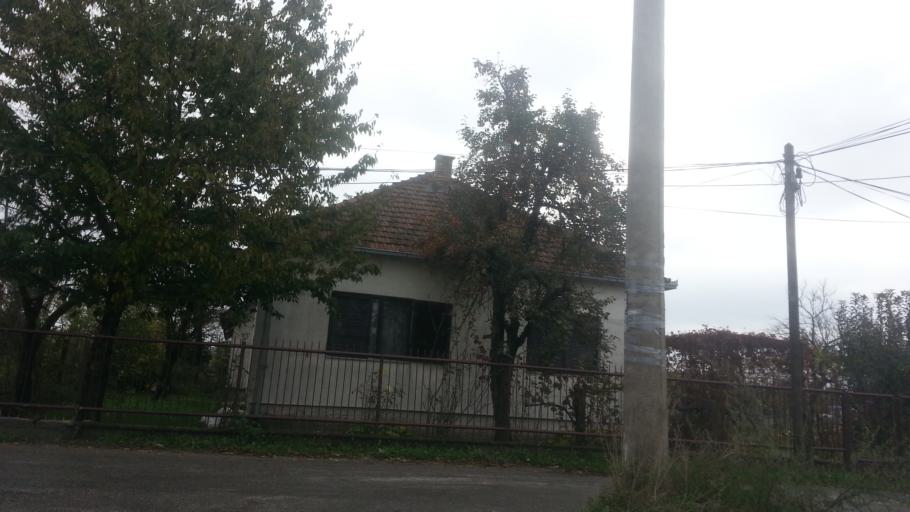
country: RS
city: Novi Banovci
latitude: 44.8974
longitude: 20.2984
